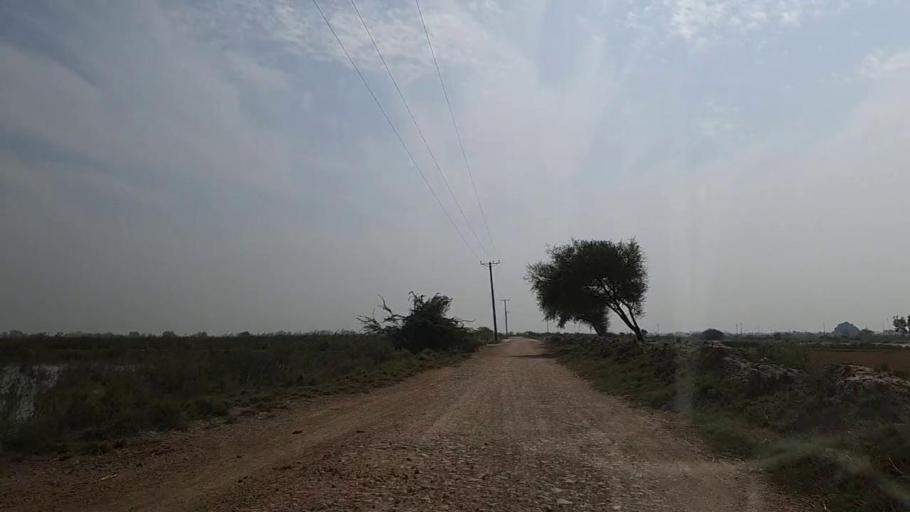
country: PK
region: Sindh
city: Mirpur Batoro
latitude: 24.6023
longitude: 68.2133
